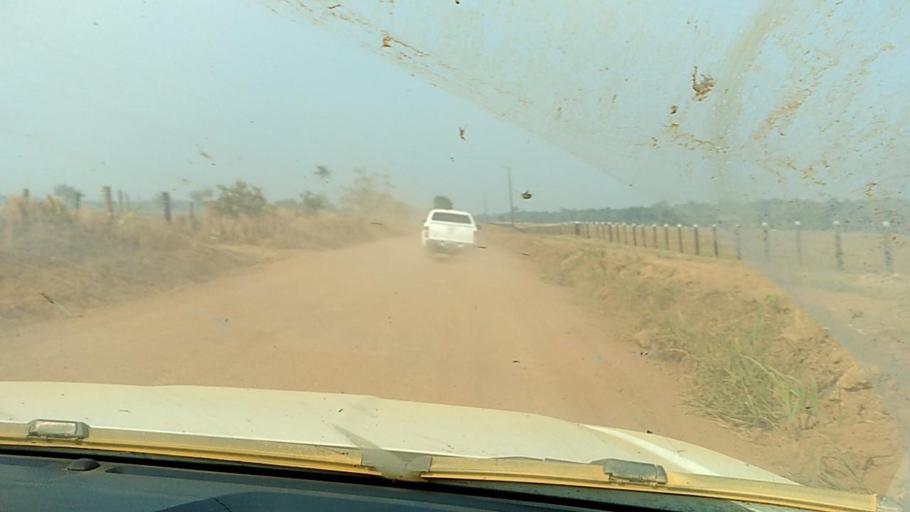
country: BR
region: Rondonia
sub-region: Porto Velho
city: Porto Velho
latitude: -8.7738
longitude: -64.0810
